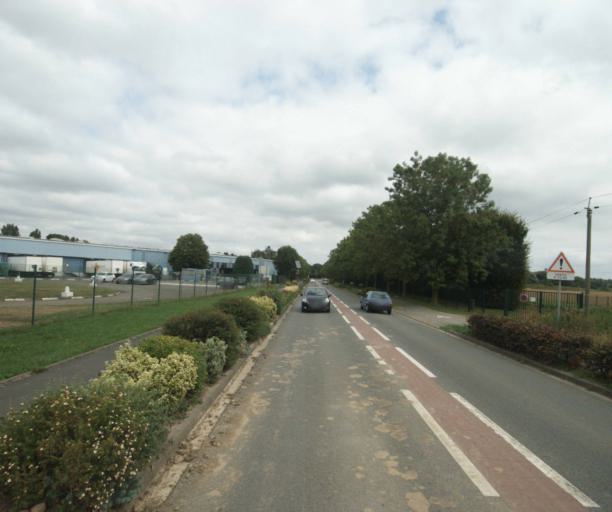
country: FR
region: Nord-Pas-de-Calais
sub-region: Departement du Nord
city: Villeneuve-d'Ascq
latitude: 50.6195
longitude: 3.1776
